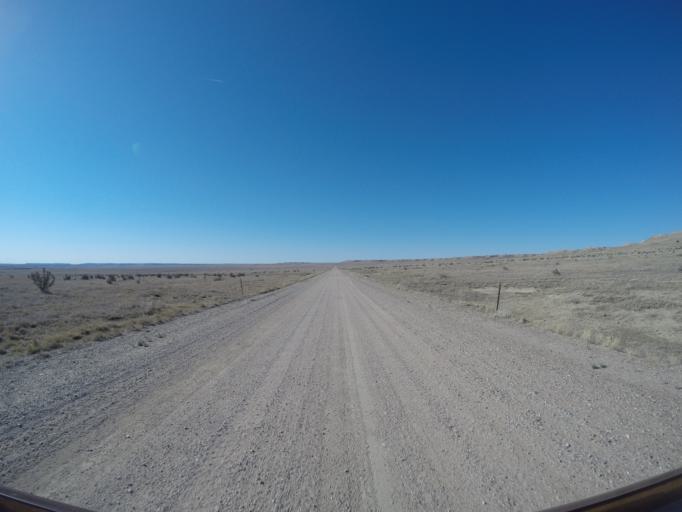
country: US
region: Colorado
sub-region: Otero County
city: La Junta
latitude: 37.7555
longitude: -103.5945
